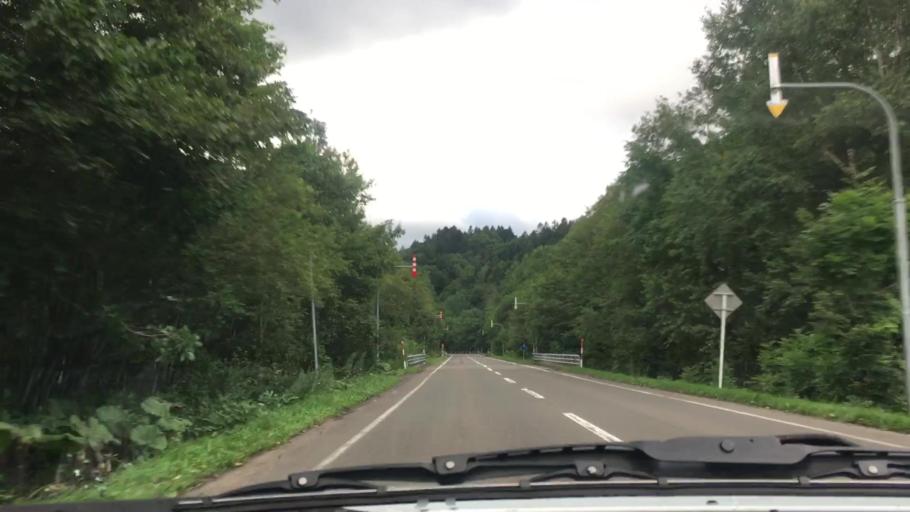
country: JP
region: Hokkaido
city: Shimo-furano
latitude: 43.0715
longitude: 142.6703
